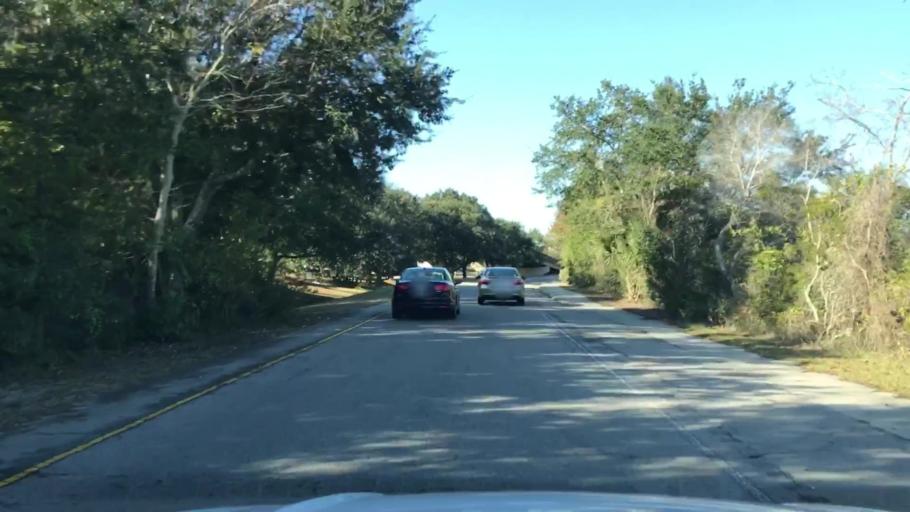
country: US
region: South Carolina
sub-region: Charleston County
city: Charleston
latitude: 32.7810
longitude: -79.9682
